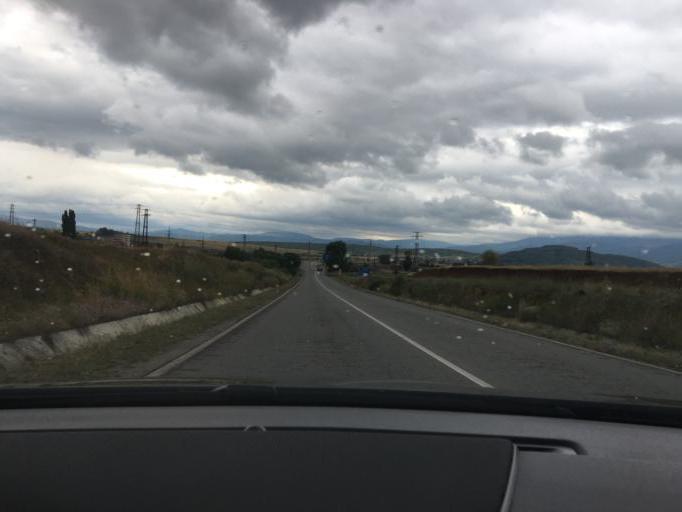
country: BG
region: Kyustendil
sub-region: Obshtina Kyustendil
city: Kyustendil
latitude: 42.2907
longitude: 22.7211
